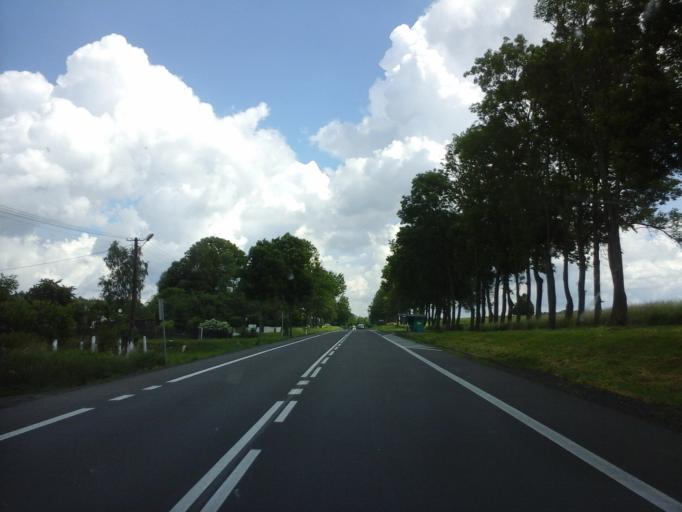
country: PL
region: West Pomeranian Voivodeship
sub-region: Powiat bialogardzki
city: Karlino
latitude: 54.0153
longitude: 15.8248
